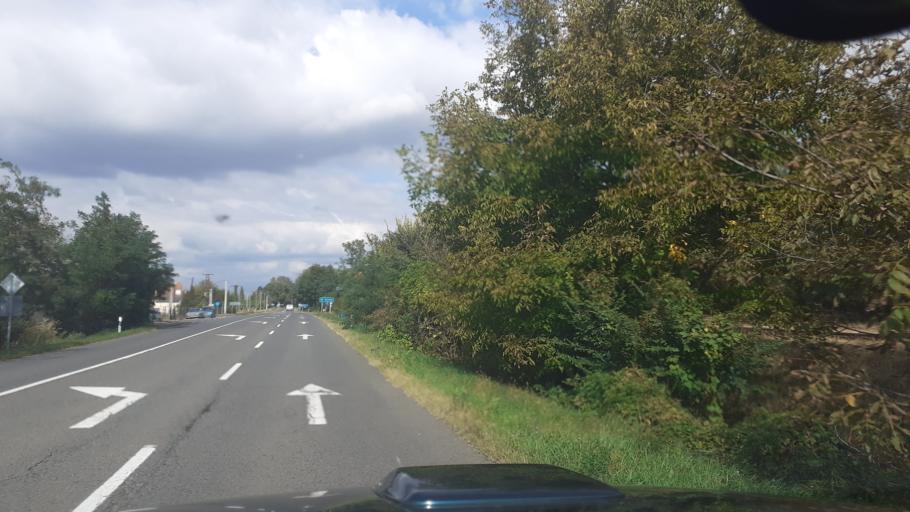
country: HU
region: Bacs-Kiskun
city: Apostag
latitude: 46.8843
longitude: 18.9774
